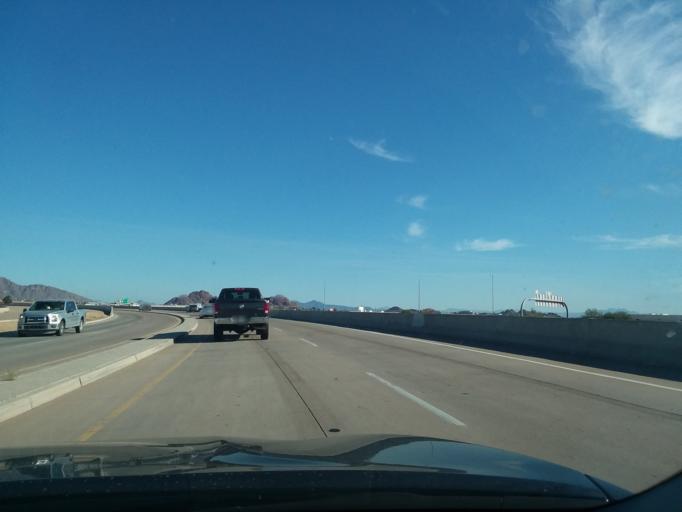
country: US
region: Arizona
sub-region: Maricopa County
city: Tempe Junction
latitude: 33.4305
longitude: -111.9809
